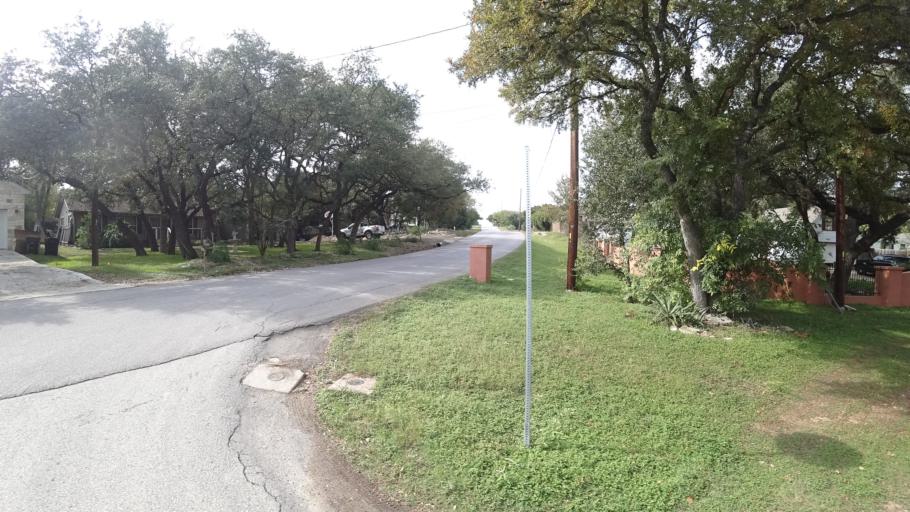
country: US
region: Texas
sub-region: Travis County
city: Hudson Bend
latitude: 30.3770
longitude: -97.9287
